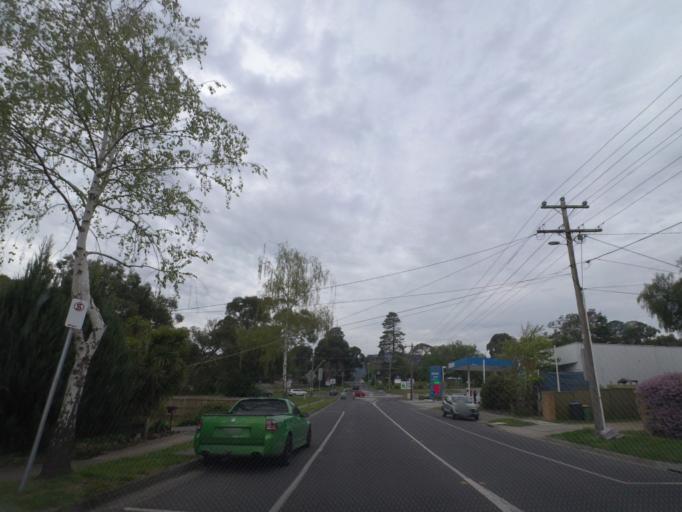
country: AU
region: Victoria
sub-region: Knox
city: The Basin
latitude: -37.8503
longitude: 145.3061
